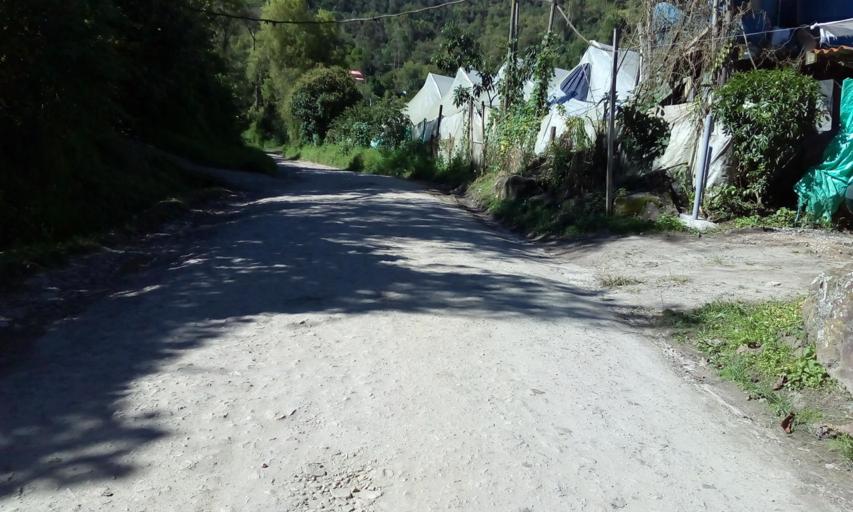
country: CO
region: Cundinamarca
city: Tenza
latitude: 5.1000
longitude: -73.4448
